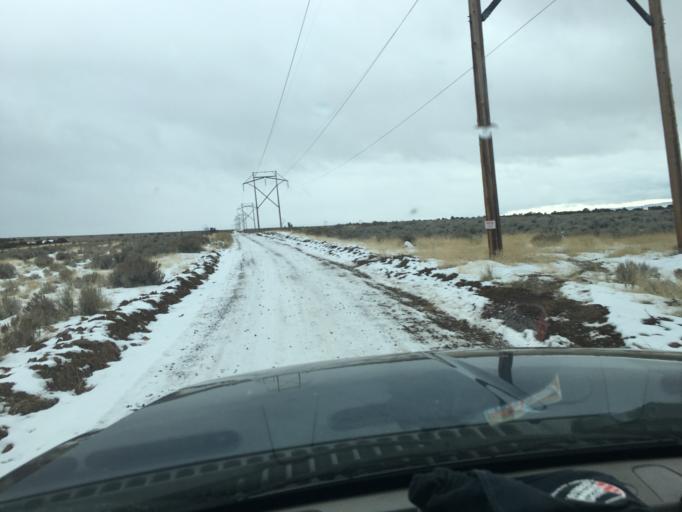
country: US
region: Colorado
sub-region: Garfield County
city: Parachute
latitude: 39.3431
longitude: -108.1699
